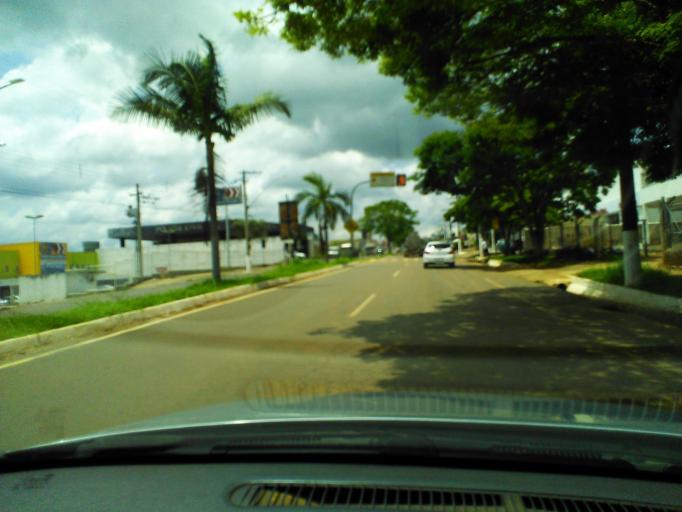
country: BR
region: Minas Gerais
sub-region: Tres Coracoes
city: Tres Coracoes
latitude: -21.6780
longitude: -45.2683
